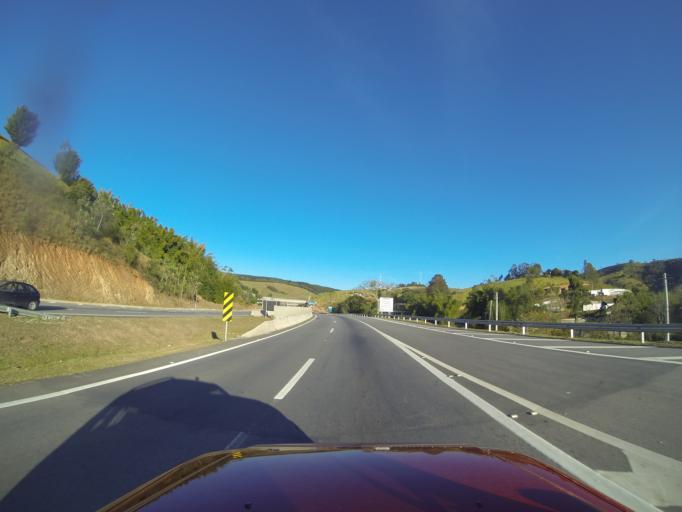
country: BR
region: Sao Paulo
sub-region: Sao Jose Dos Campos
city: Sao Jose dos Campos
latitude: -23.2762
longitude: -45.8121
